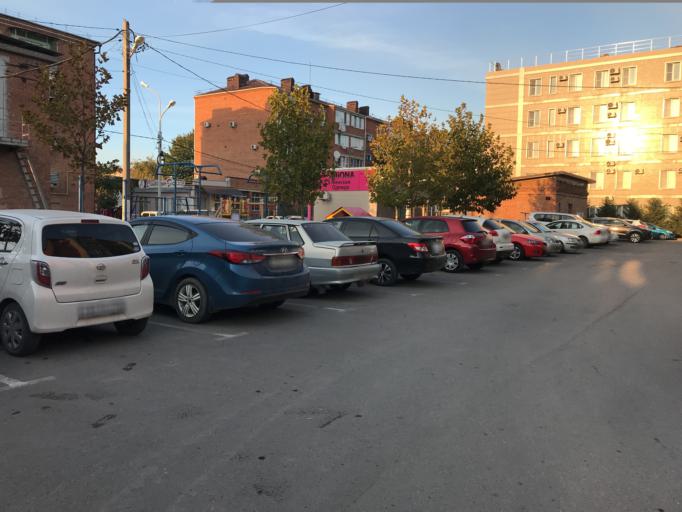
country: RU
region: Krasnodarskiy
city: Slavyansk-na-Kubani
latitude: 45.2581
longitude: 38.1215
